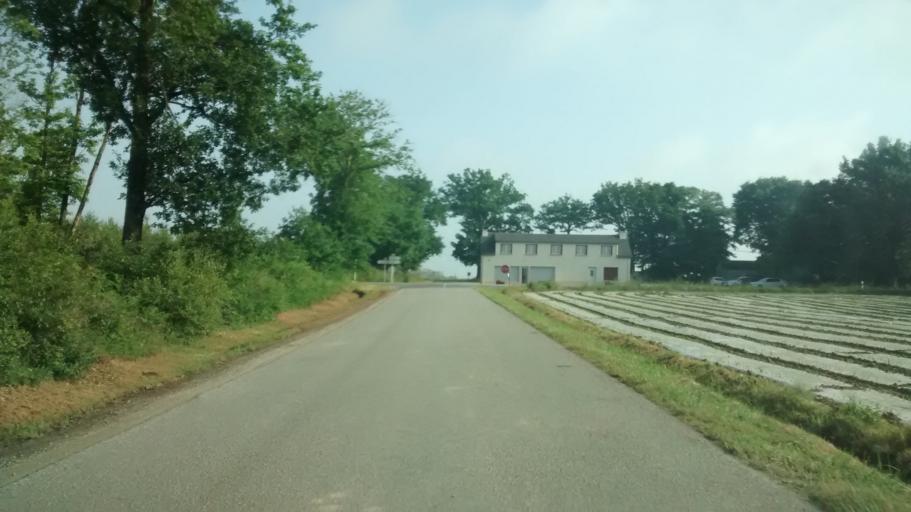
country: FR
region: Brittany
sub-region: Departement du Morbihan
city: Ruffiac
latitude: 47.8458
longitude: -2.2756
